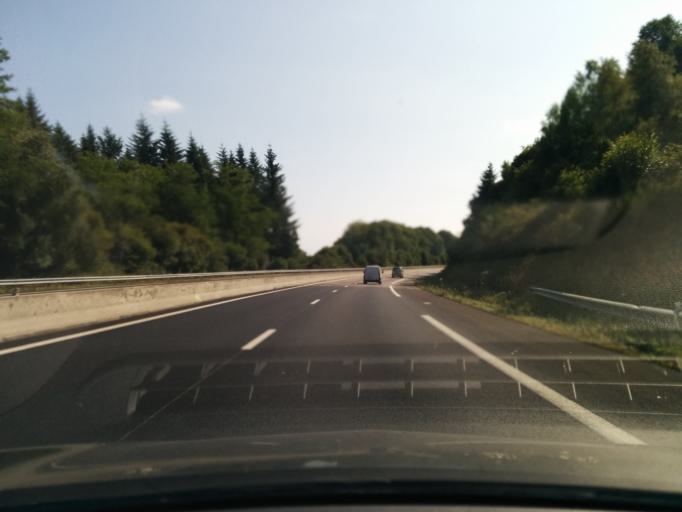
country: FR
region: Limousin
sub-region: Departement de la Haute-Vienne
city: Razes
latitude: 45.9953
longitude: 1.3362
